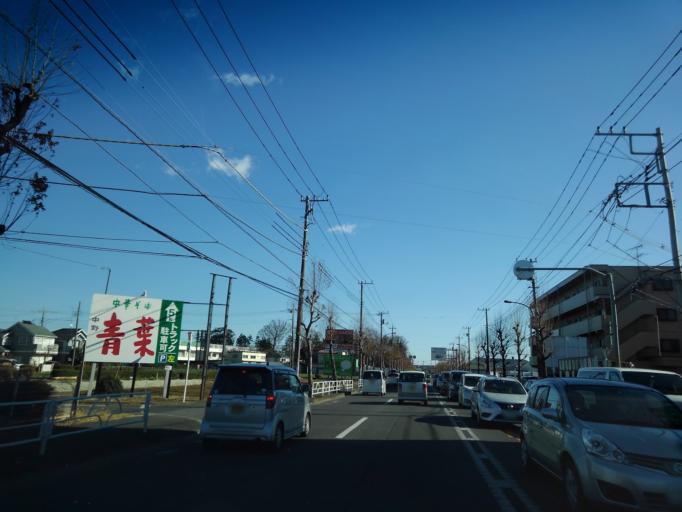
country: JP
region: Tokyo
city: Fussa
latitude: 35.7505
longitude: 139.3909
